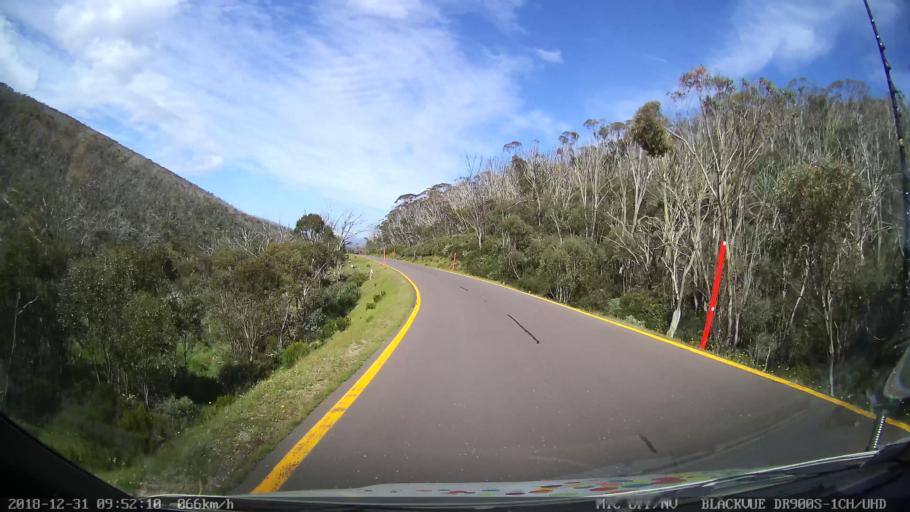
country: AU
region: New South Wales
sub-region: Snowy River
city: Jindabyne
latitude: -36.5257
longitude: 148.2559
